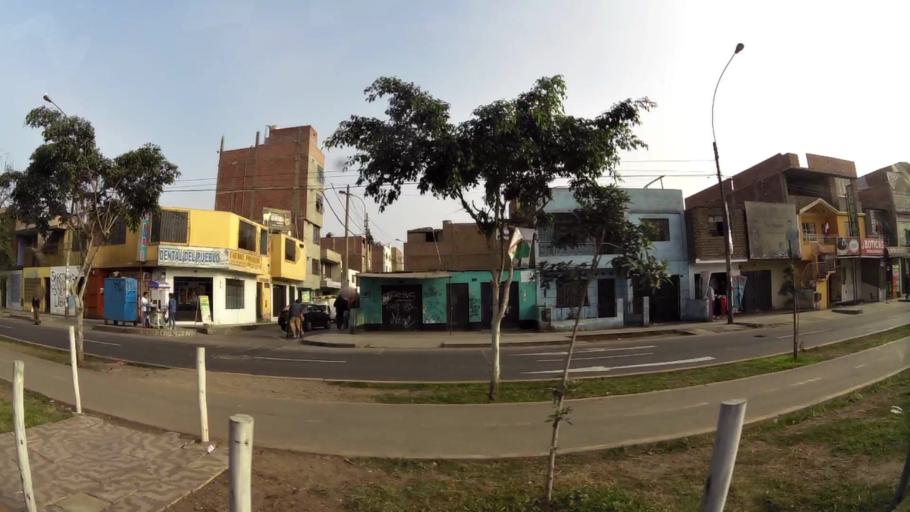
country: PE
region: Callao
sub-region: Callao
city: Callao
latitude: -12.0229
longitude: -77.0827
